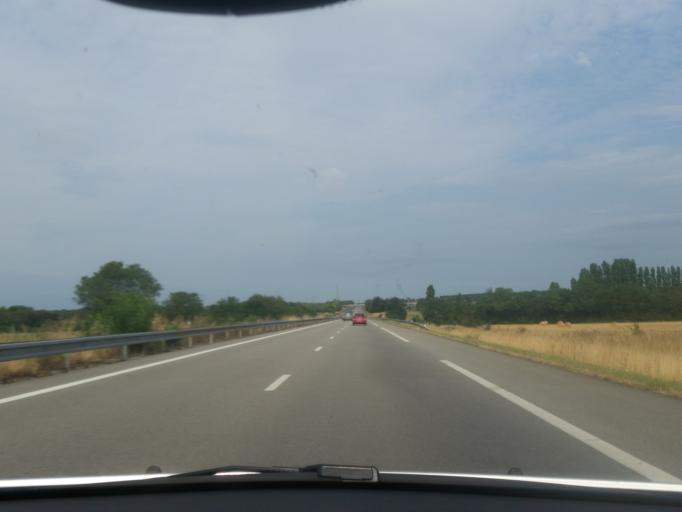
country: FR
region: Pays de la Loire
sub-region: Departement de la Loire-Atlantique
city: Saint-Herblon
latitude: 47.4145
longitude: -1.1381
